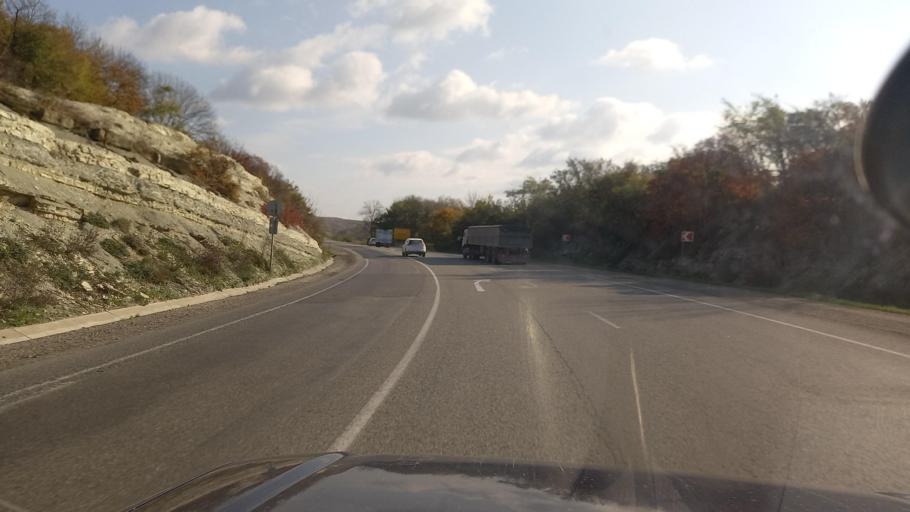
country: RU
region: Krasnodarskiy
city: Gayduk
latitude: 44.8738
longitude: 37.7691
